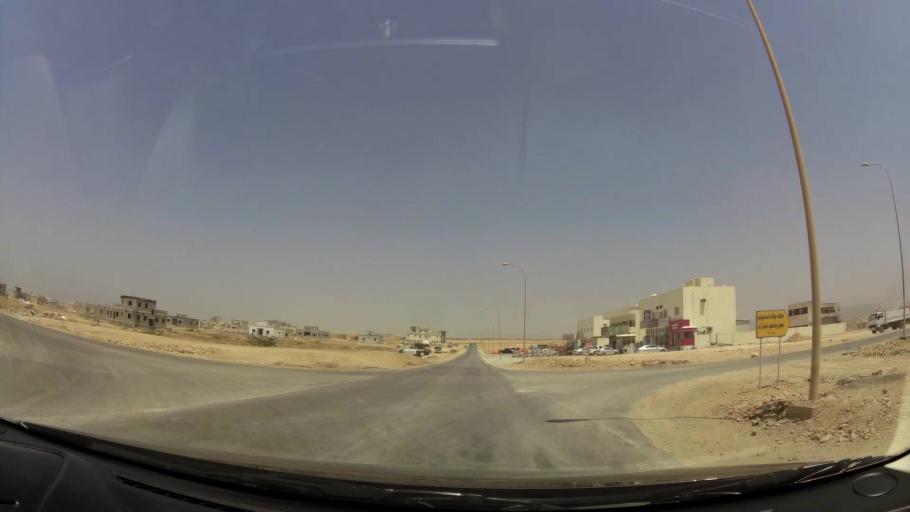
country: OM
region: Zufar
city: Salalah
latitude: 17.0821
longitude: 54.1931
